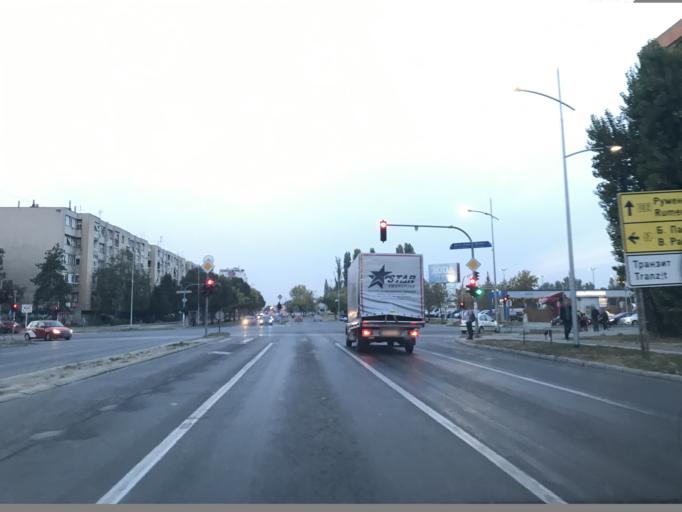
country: RS
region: Autonomna Pokrajina Vojvodina
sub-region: Juznobacki Okrug
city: Novi Sad
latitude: 45.2637
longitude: 19.8176
